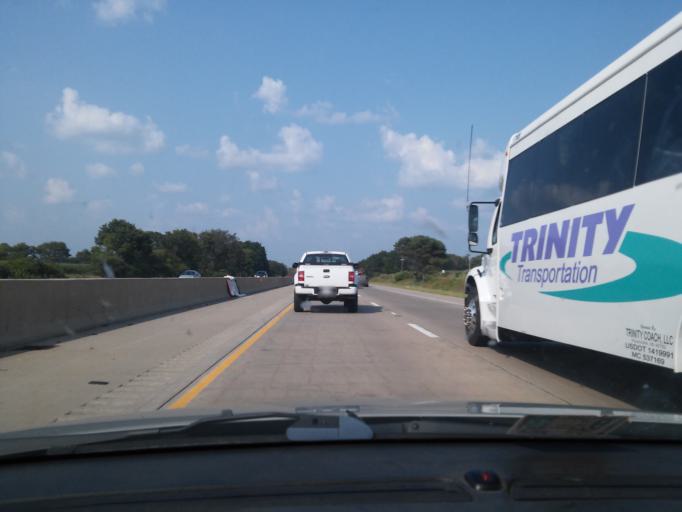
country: US
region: Illinois
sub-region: Grundy County
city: Minooka
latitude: 41.4369
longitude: -88.3398
